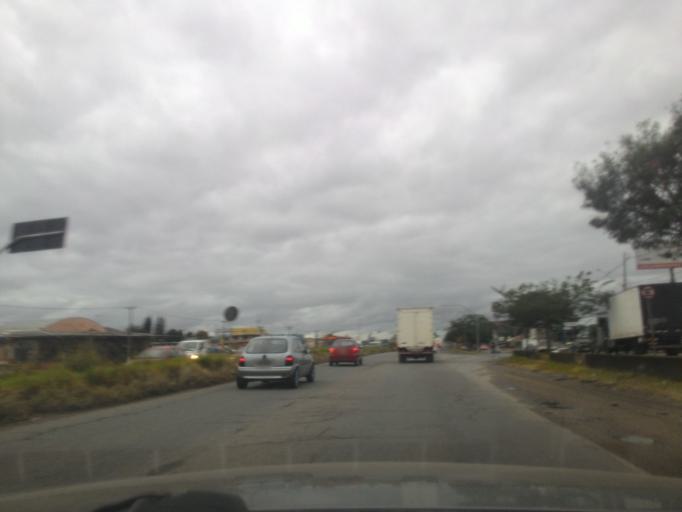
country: BR
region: Parana
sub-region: Sao Jose Dos Pinhais
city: Sao Jose dos Pinhais
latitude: -25.5278
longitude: -49.2983
